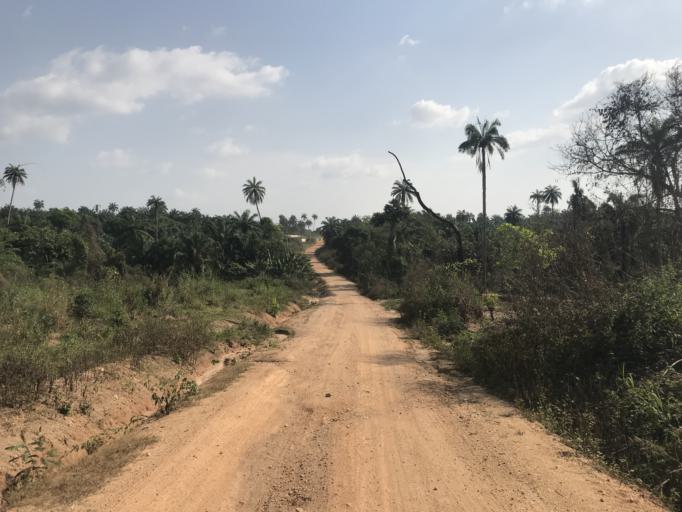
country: NG
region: Osun
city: Ikirun
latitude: 7.8648
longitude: 4.5874
